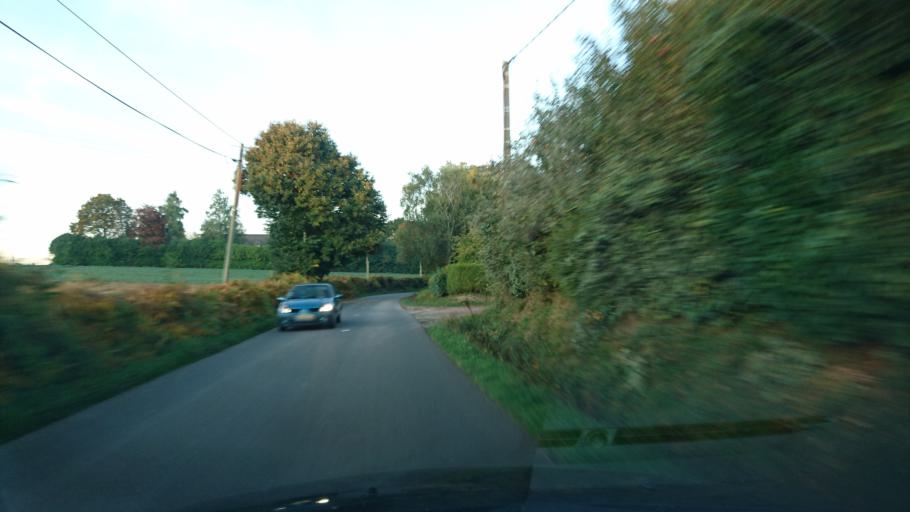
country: FR
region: Brittany
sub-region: Departement d'Ille-et-Vilaine
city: Bruz
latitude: 48.0143
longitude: -1.7594
